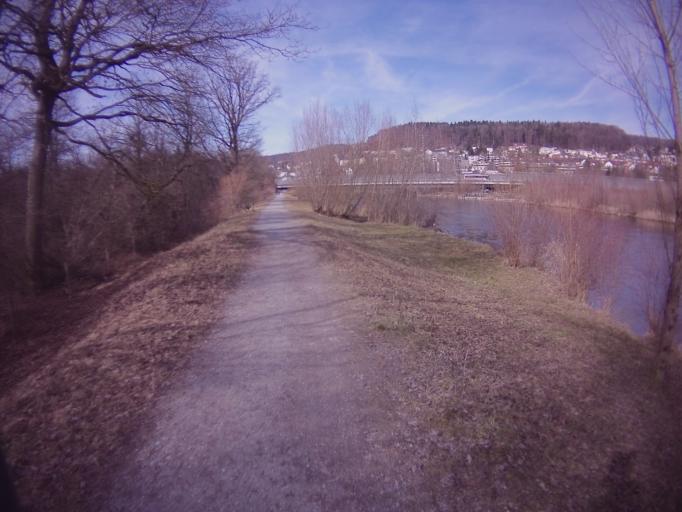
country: CH
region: Zurich
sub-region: Bezirk Dietikon
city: Geroldswil
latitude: 47.4194
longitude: 8.4032
